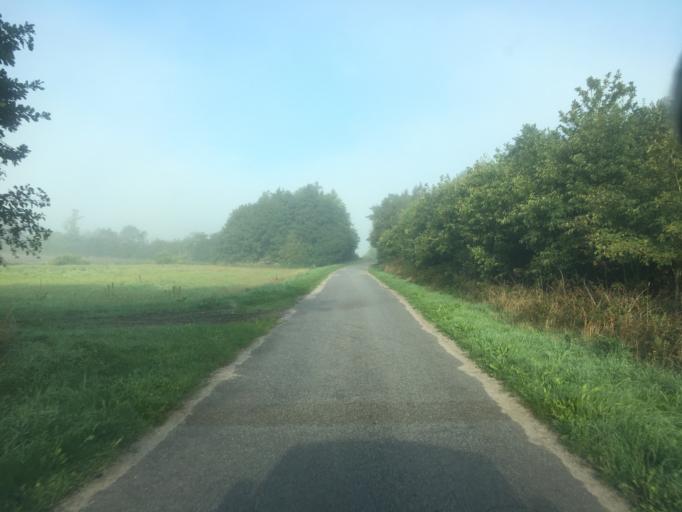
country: DK
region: South Denmark
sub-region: Tonder Kommune
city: Logumkloster
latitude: 55.0212
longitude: 8.8997
